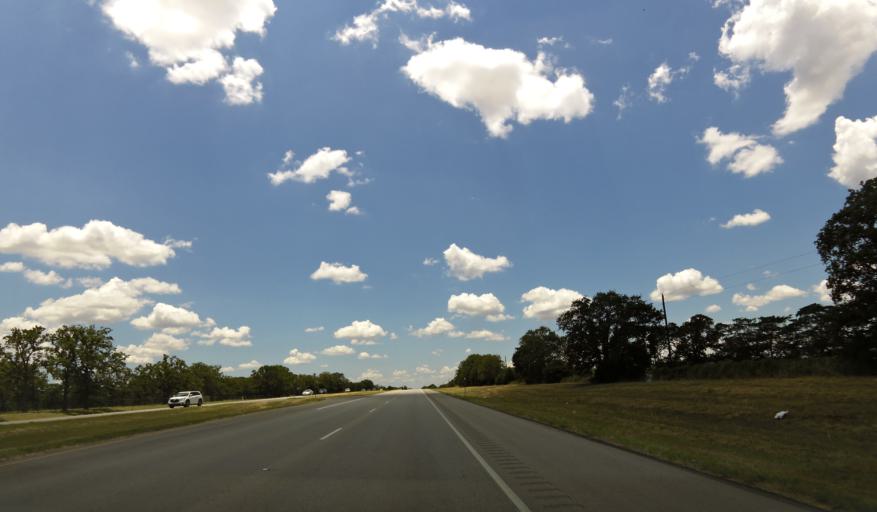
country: US
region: Texas
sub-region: Lee County
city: Giddings
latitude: 30.1471
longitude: -96.7090
